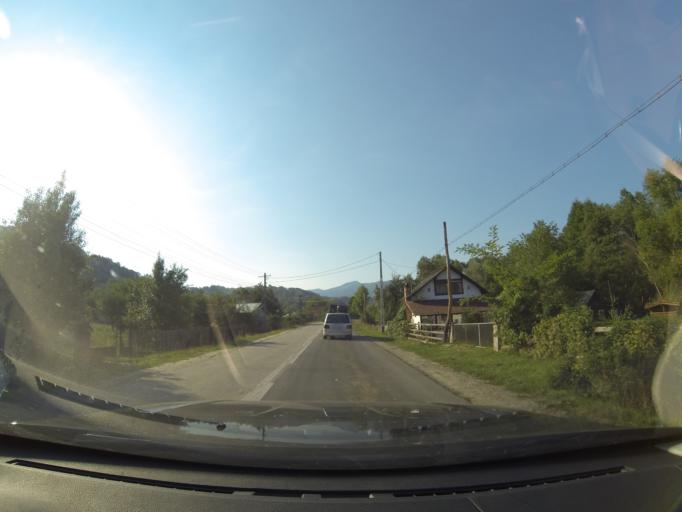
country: RO
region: Arges
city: Poenari
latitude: 45.3193
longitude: 24.6413
